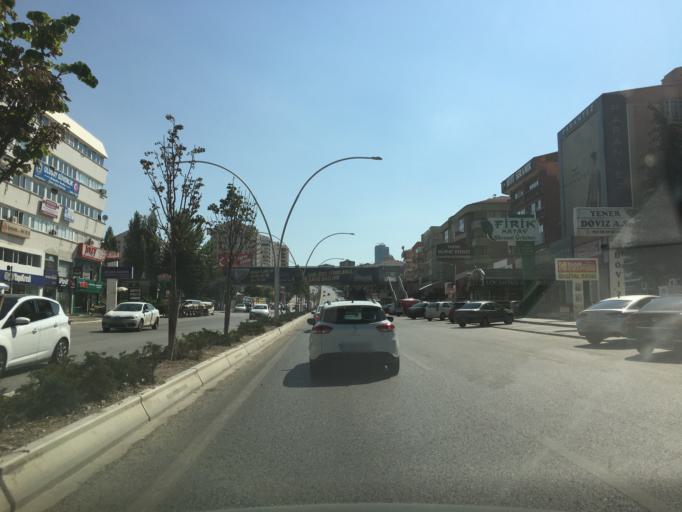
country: TR
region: Ankara
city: Cankaya
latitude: 39.8740
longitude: 32.8625
